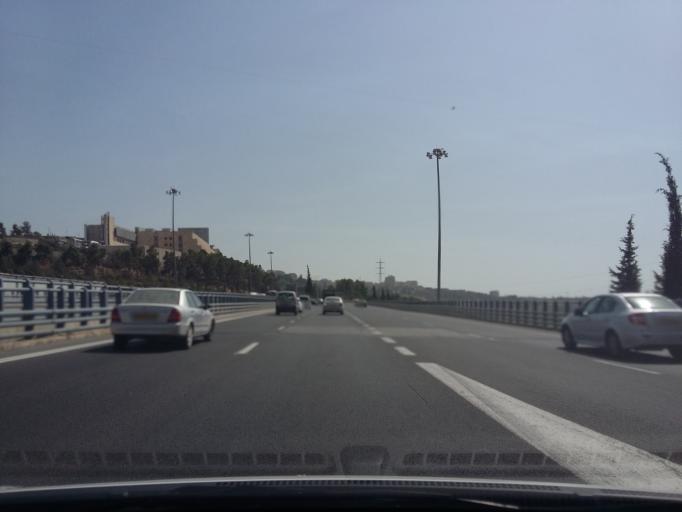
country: IL
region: Jerusalem
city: West Jerusalem
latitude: 31.8089
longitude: 35.2087
